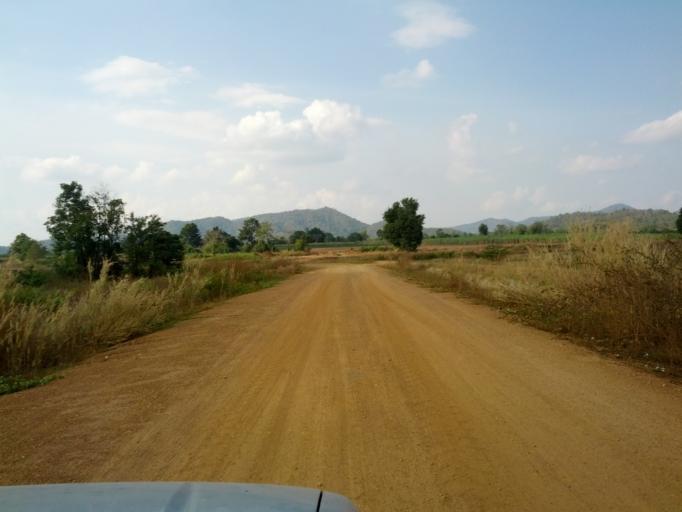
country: TH
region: Sukhothai
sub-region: Amphoe Si Satchanalai
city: Si Satchanalai
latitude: 17.4674
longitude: 99.7041
